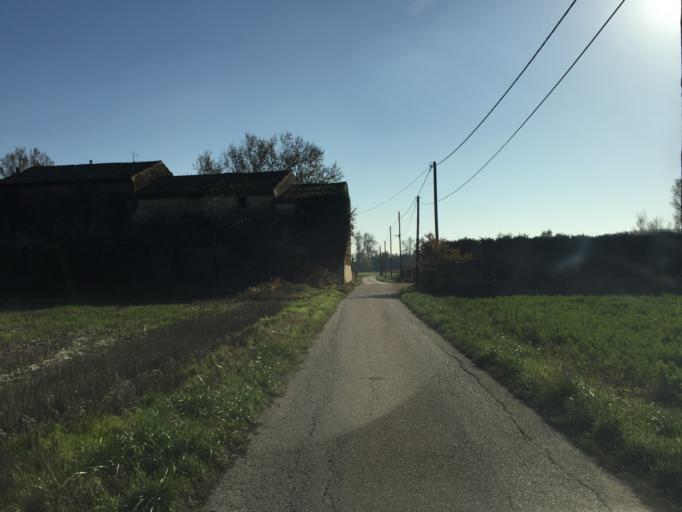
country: FR
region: Provence-Alpes-Cote d'Azur
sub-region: Departement du Vaucluse
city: Bedarrides
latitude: 44.0368
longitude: 4.9036
